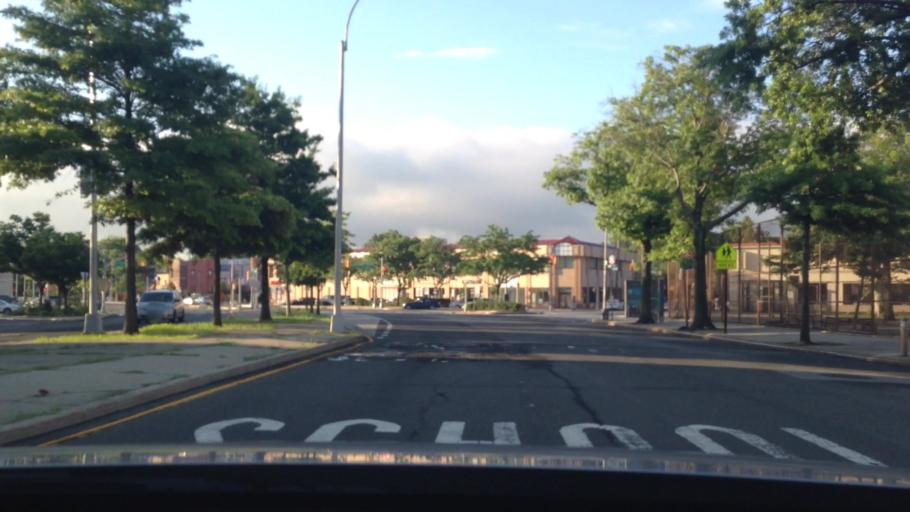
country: US
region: New York
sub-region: Nassau County
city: East Atlantic Beach
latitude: 40.7650
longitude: -73.7889
